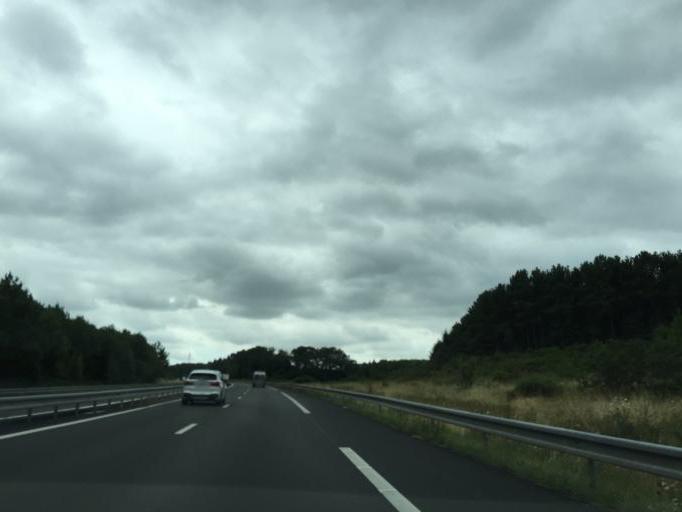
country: FR
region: Pays de la Loire
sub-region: Departement de la Sarthe
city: Ecommoy
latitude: 47.8572
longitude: 0.2974
